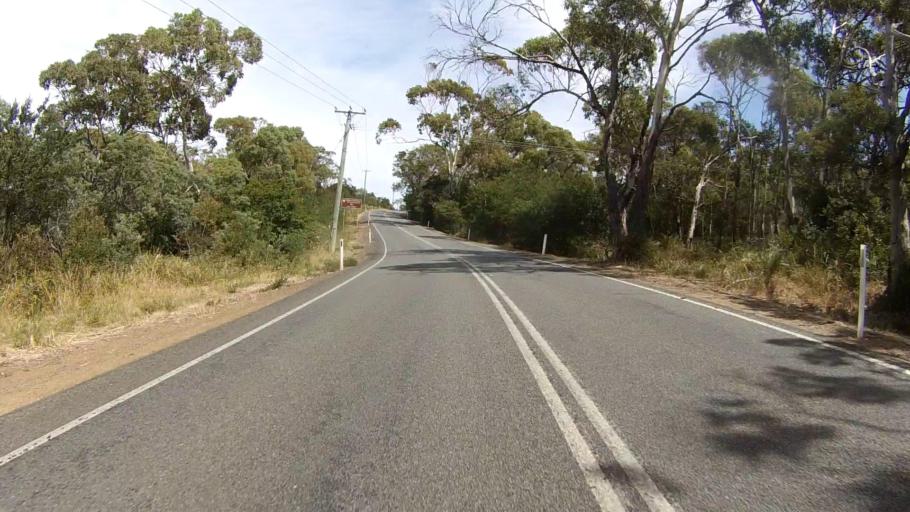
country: AU
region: Tasmania
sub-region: Clarence
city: Sandford
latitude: -43.0250
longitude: 147.4833
